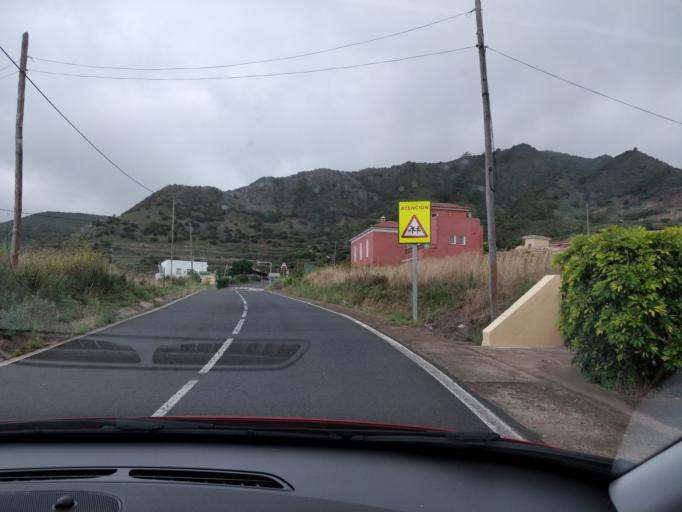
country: ES
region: Canary Islands
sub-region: Provincia de Santa Cruz de Tenerife
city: Tanque
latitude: 28.3288
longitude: -16.8467
